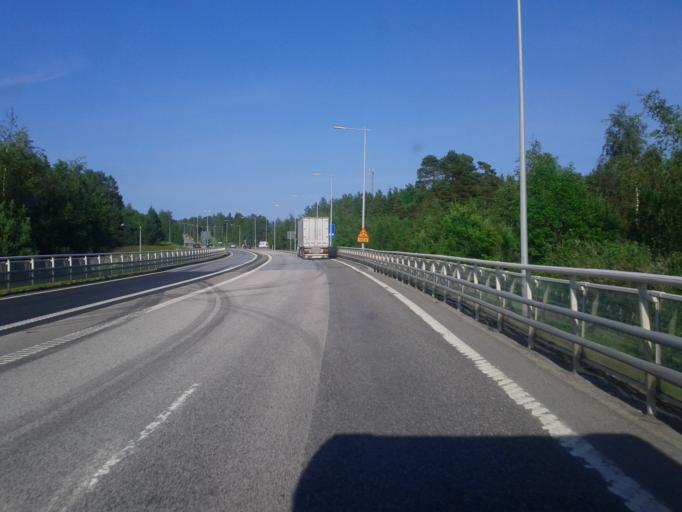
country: SE
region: Vaesterbotten
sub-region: Umea Kommun
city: Umea
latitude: 63.8015
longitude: 20.3066
